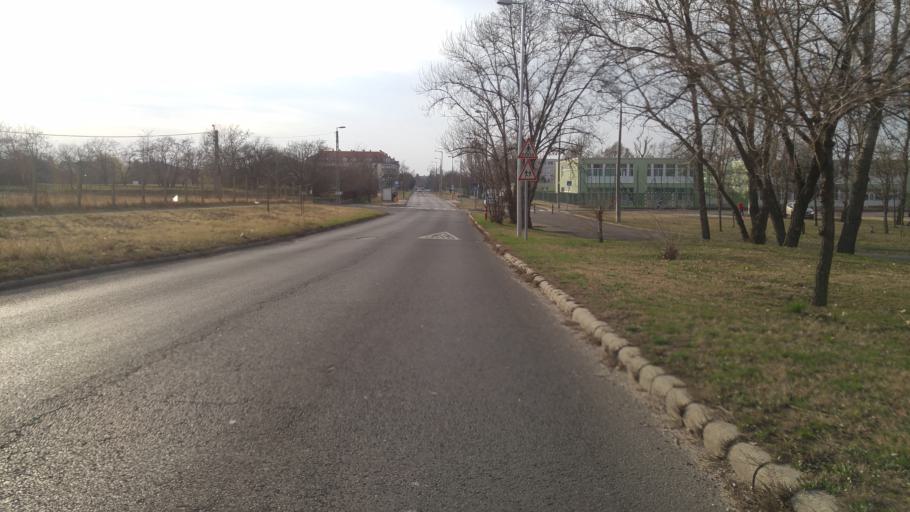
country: HU
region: Budapest
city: Budapest XVII. keruelet
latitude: 47.4786
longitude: 19.2386
